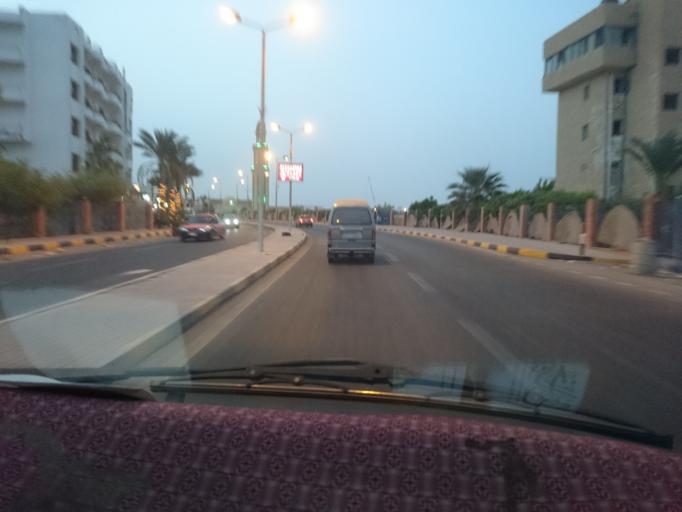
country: EG
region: Red Sea
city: Hurghada
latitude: 27.2374
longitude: 33.8463
